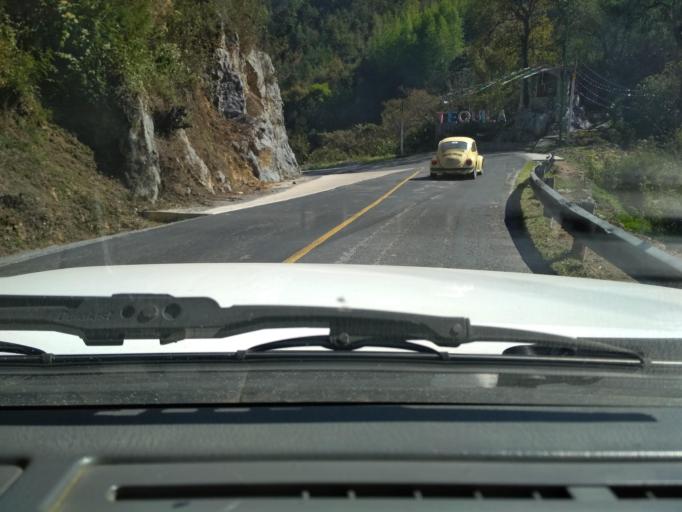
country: MX
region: Veracruz
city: Tequila
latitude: 18.7455
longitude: -97.0897
